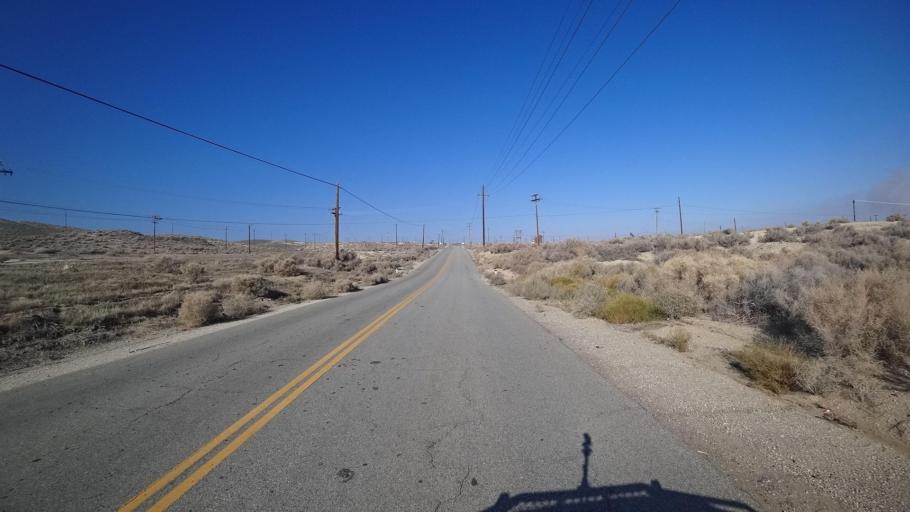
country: US
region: California
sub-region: Kern County
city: Taft Heights
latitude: 35.1983
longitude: -119.5898
